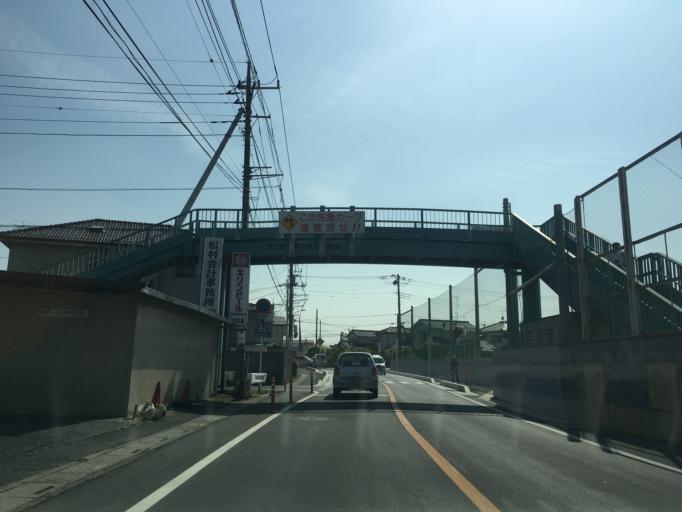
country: JP
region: Saitama
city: Sugito
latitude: 36.0225
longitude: 139.7330
